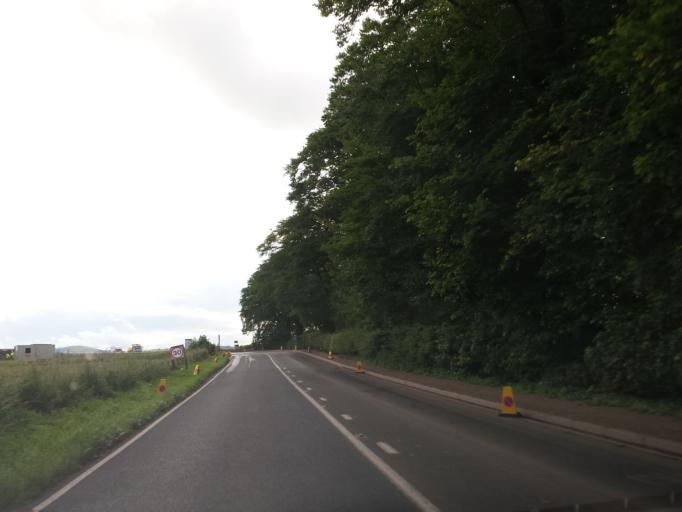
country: GB
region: Scotland
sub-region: Fife
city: Leuchars
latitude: 56.3597
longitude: -2.8988
